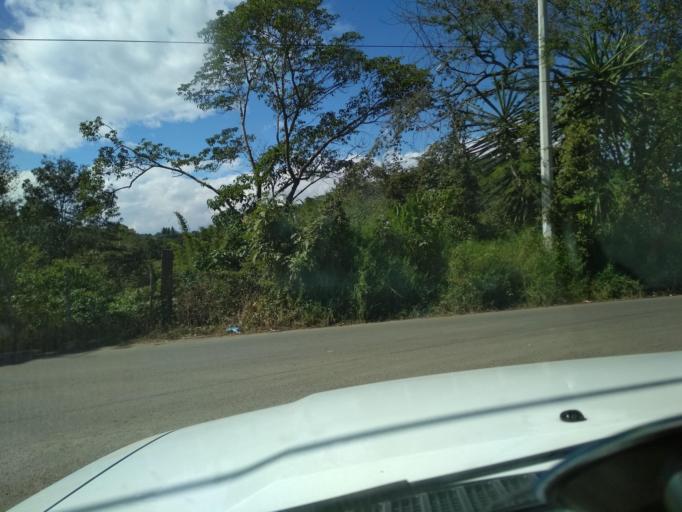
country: MX
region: Veracruz
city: El Castillo
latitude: 19.5524
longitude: -96.8569
